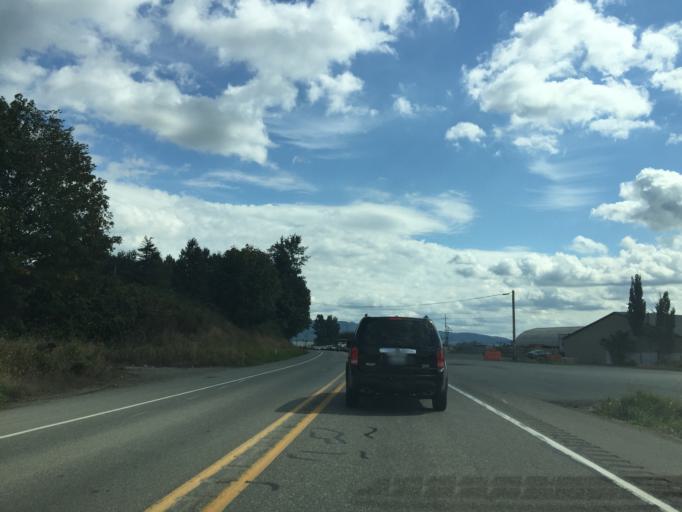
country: US
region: Washington
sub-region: Snohomish County
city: Monroe
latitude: 47.8768
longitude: -122.0166
